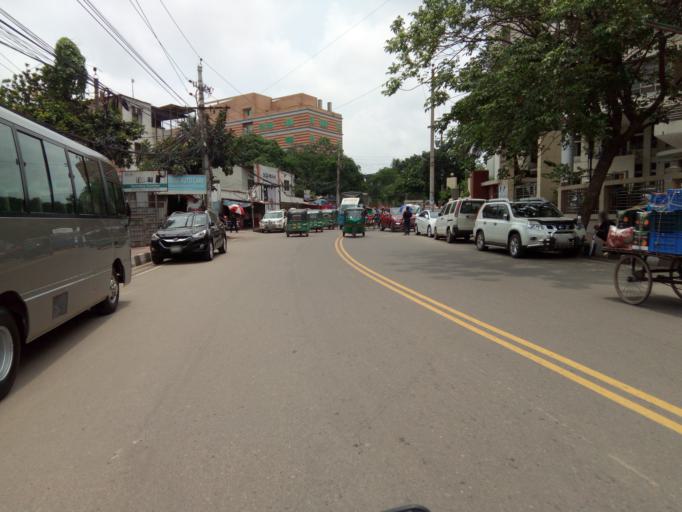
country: BD
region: Dhaka
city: Paltan
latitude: 23.7634
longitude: 90.4060
